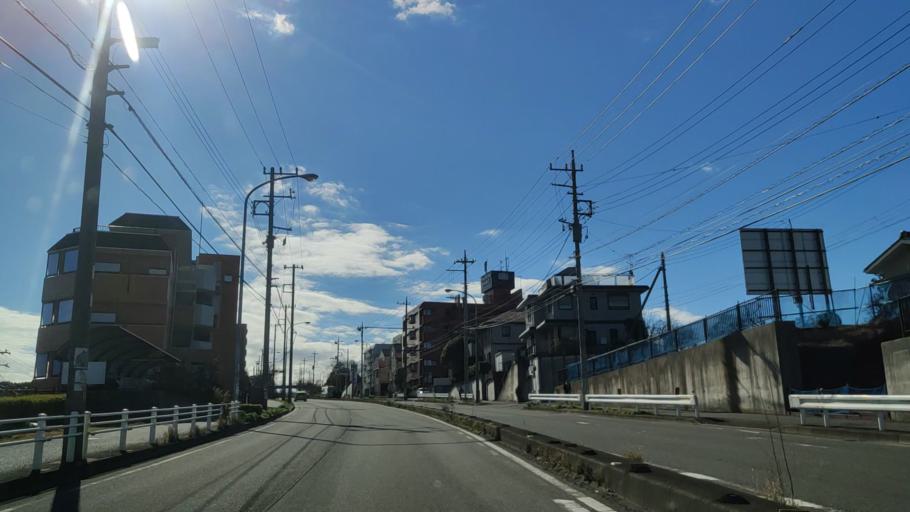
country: JP
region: Kanagawa
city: Minami-rinkan
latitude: 35.5068
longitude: 139.5433
